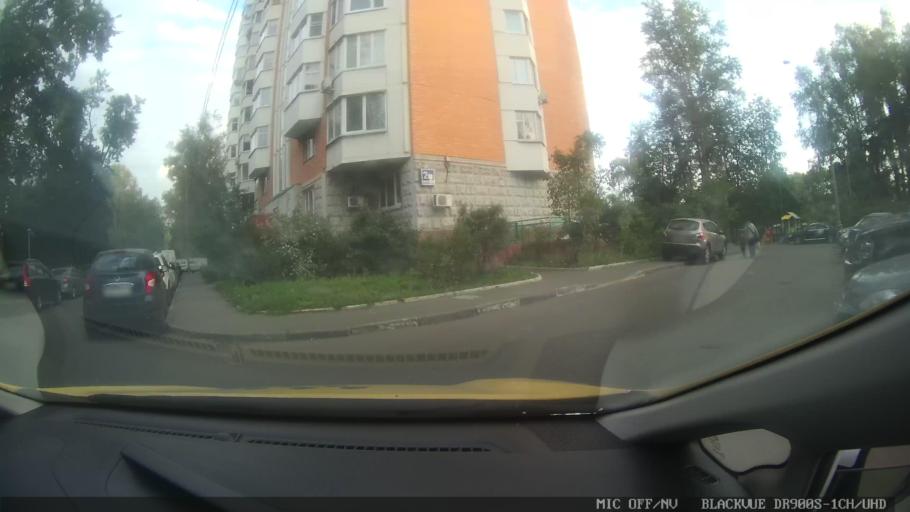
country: RU
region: Moscow
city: Vatutino
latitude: 55.8577
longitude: 37.6984
